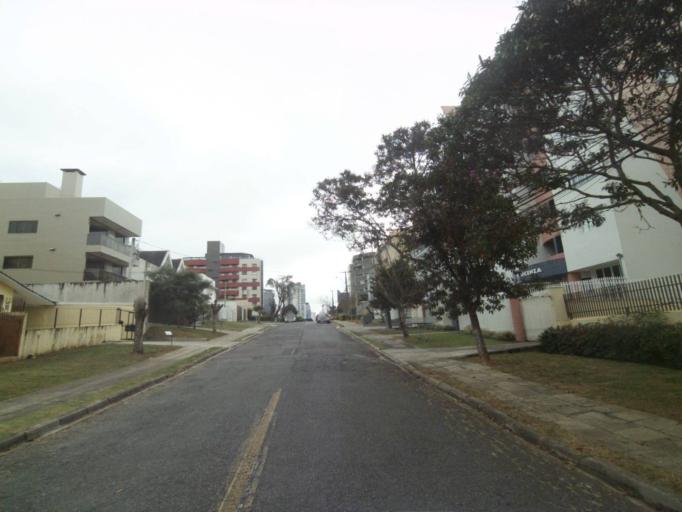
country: BR
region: Parana
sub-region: Curitiba
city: Curitiba
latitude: -25.4565
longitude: -49.2955
